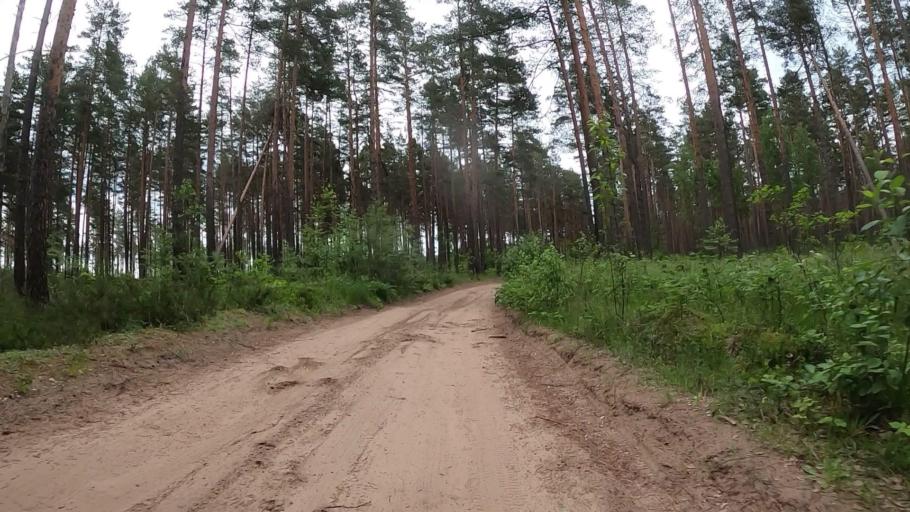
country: LV
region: Riga
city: Bergi
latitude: 57.0214
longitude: 24.2473
